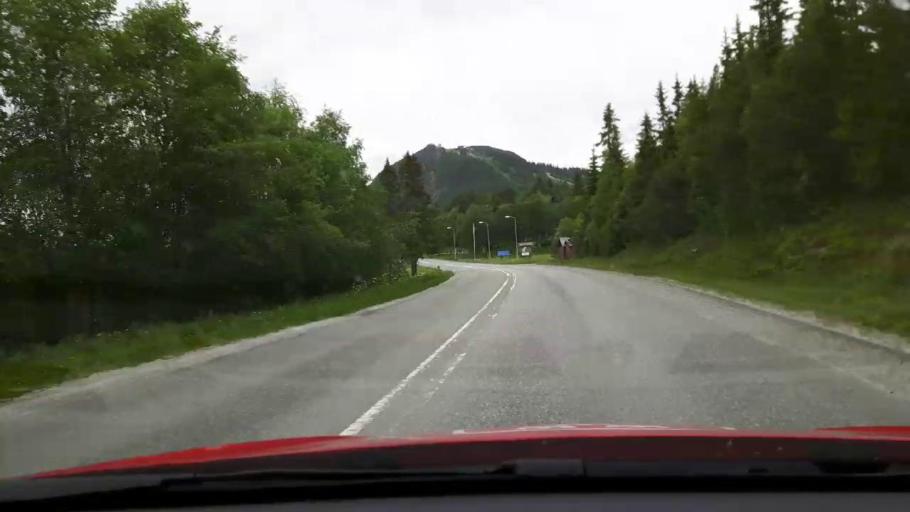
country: NO
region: Hedmark
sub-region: Engerdal
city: Engerdal
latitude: 62.5357
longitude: 12.5578
